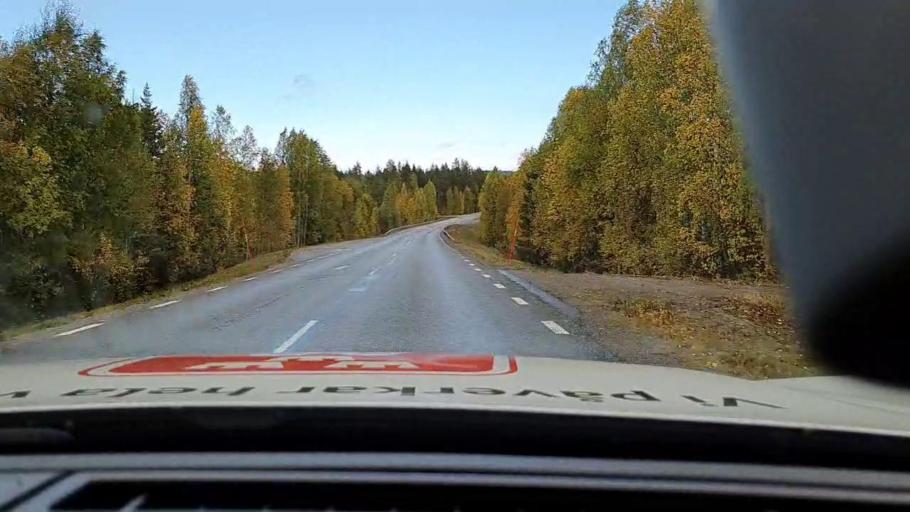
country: SE
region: Vaesterbotten
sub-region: Norsjo Kommun
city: Norsjoe
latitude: 64.9608
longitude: 19.6950
